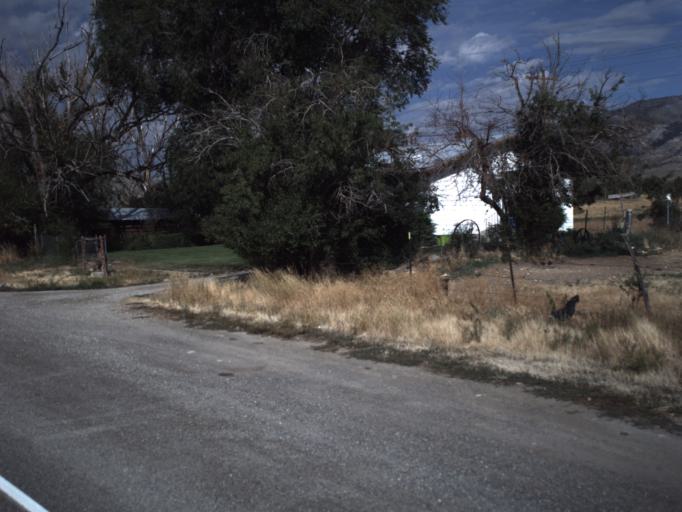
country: US
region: Idaho
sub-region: Cassia County
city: Burley
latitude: 41.8185
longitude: -113.4132
